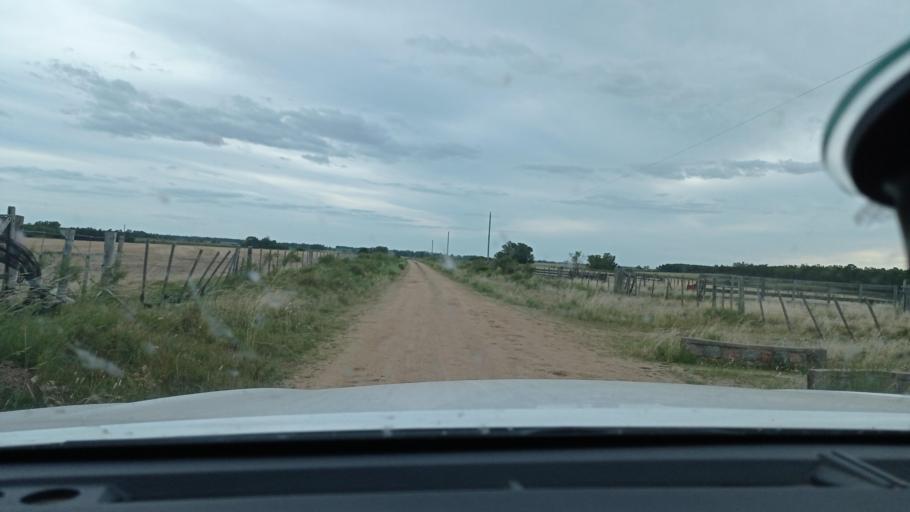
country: UY
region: Florida
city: Casupa
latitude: -34.1373
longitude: -55.8022
